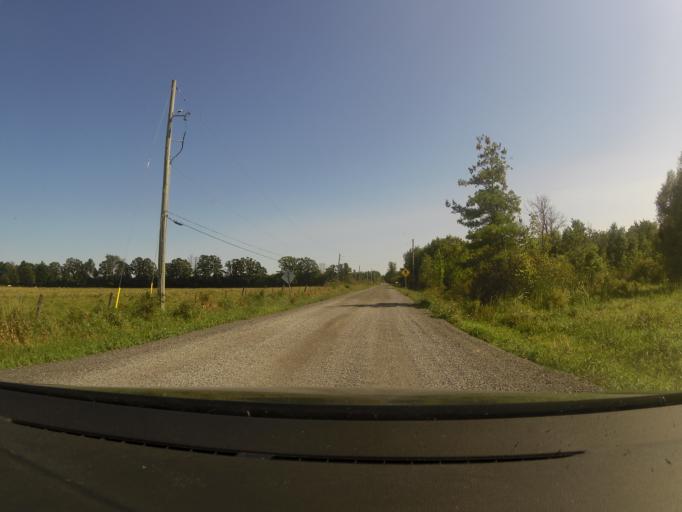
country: CA
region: Ontario
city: Carleton Place
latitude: 45.3297
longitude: -76.0874
